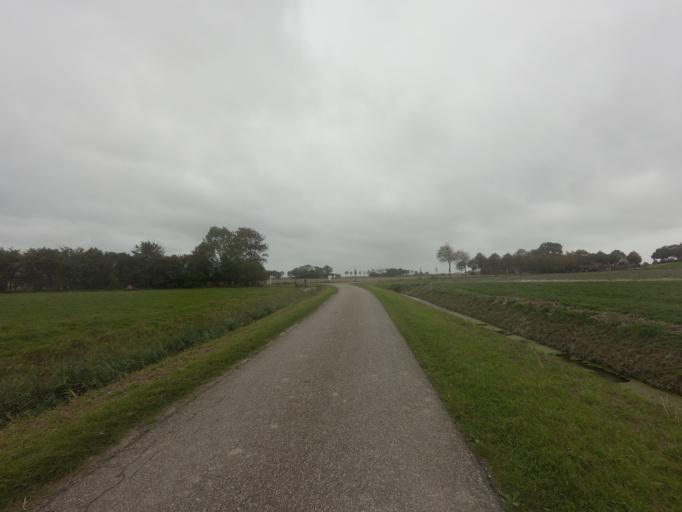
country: NL
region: Friesland
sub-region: Gemeente Ferwerderadiel
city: Ferwert
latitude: 53.3366
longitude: 5.8556
